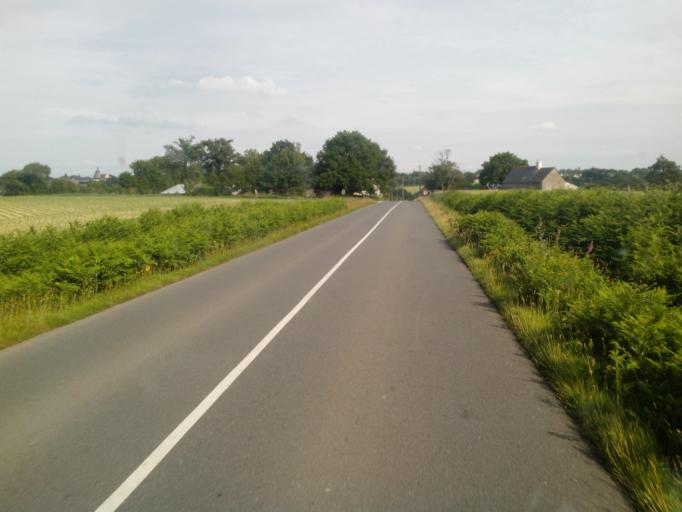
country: FR
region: Brittany
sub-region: Departement d'Ille-et-Vilaine
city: Plelan-le-Grand
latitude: 48.0059
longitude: -2.1195
